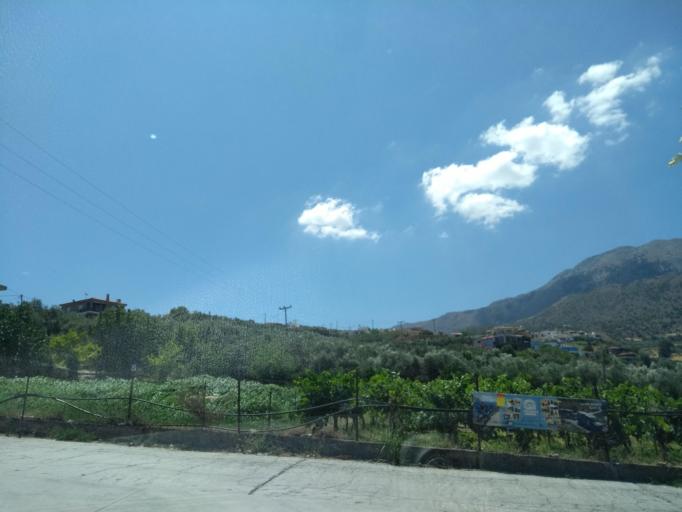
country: GR
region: Crete
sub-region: Nomos Chanias
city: Georgioupolis
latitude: 35.3329
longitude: 24.2808
